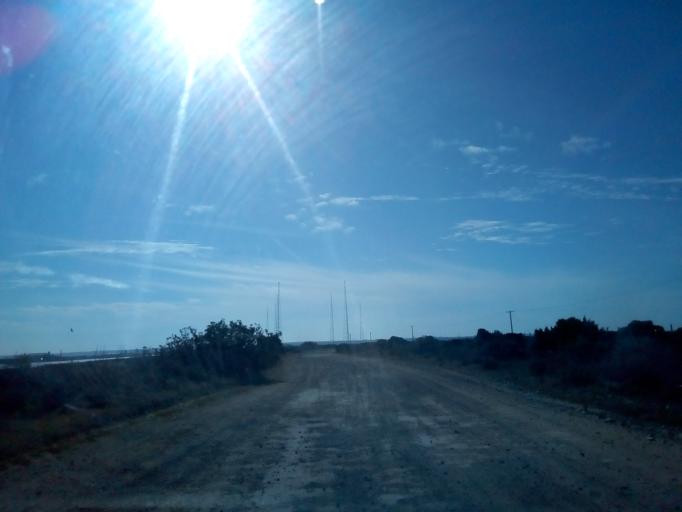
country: CY
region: Limassol
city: Limassol
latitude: 34.6304
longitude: 33.0049
